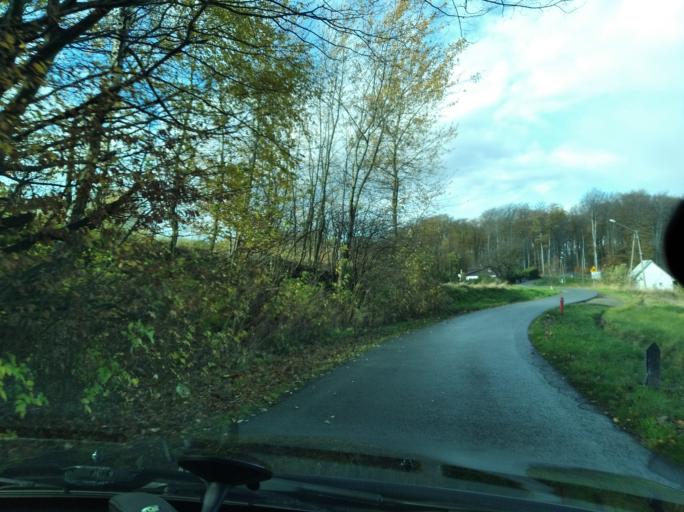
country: PL
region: Subcarpathian Voivodeship
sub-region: Powiat debicki
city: Debica
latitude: 50.0300
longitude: 21.4589
